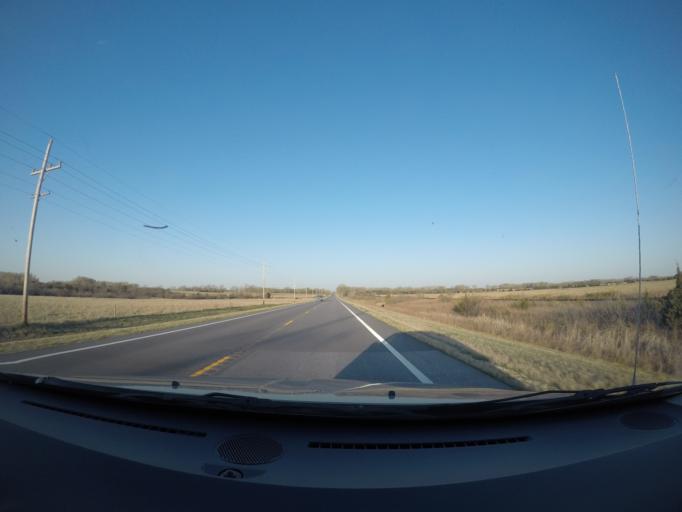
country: US
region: Kansas
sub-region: Stafford County
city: Stafford
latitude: 37.8338
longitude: -98.3731
